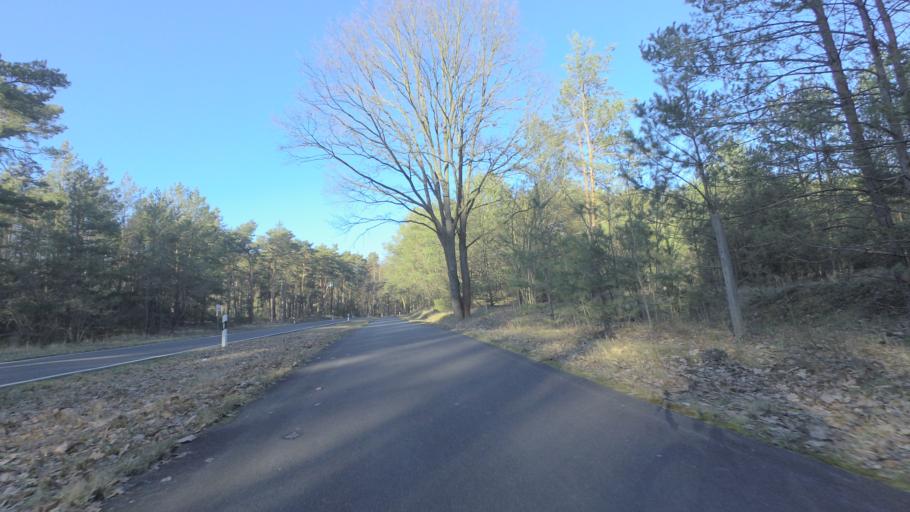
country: DE
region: Brandenburg
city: Sperenberg
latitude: 52.0368
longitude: 13.3189
